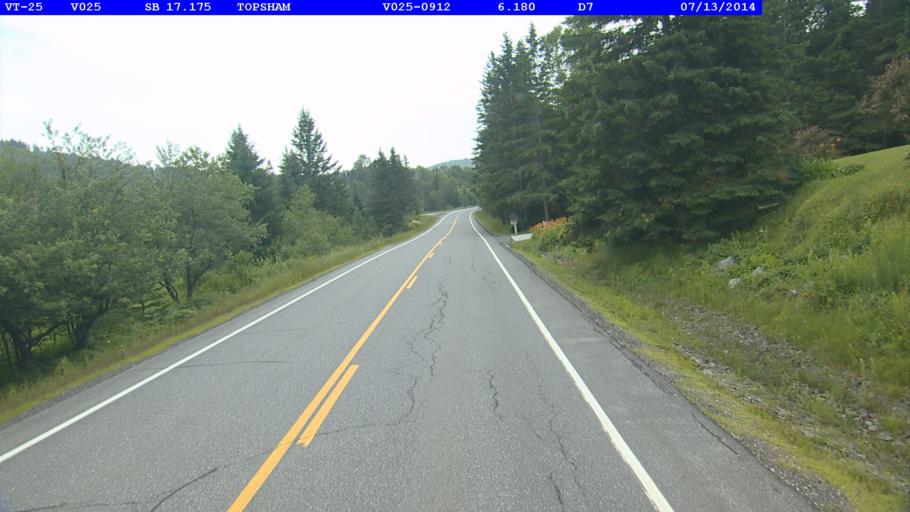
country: US
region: Vermont
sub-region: Washington County
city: South Barre
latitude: 44.1335
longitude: -72.3155
